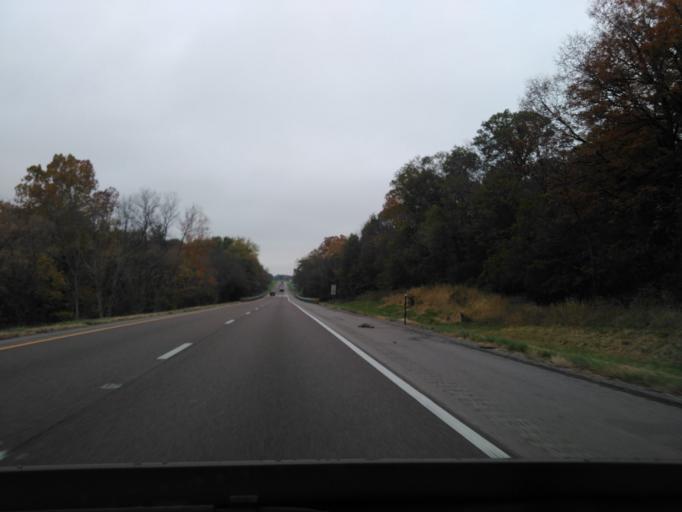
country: US
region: Illinois
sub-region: Madison County
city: Saint Jacob
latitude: 38.7705
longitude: -89.7509
